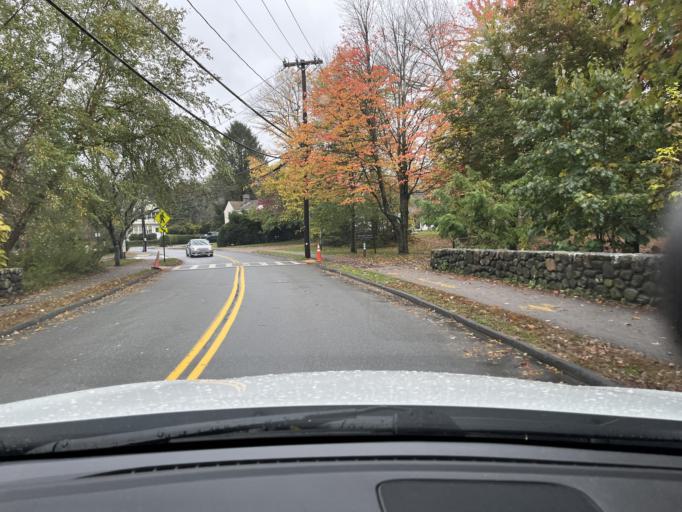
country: US
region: Massachusetts
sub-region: Norfolk County
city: Wellesley
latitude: 42.3009
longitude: -71.2849
